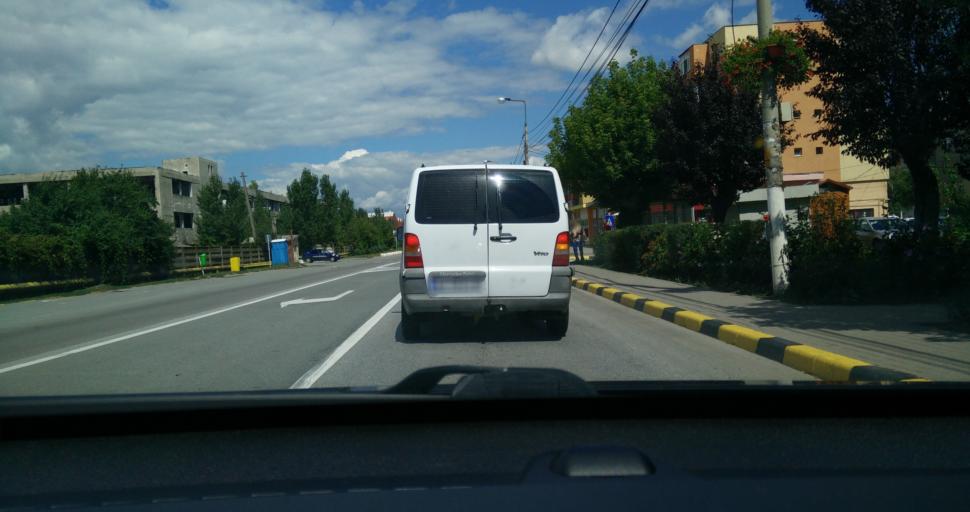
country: RO
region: Alba
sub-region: Municipiul Sebes
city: Sebes
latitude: 45.9650
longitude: 23.5575
